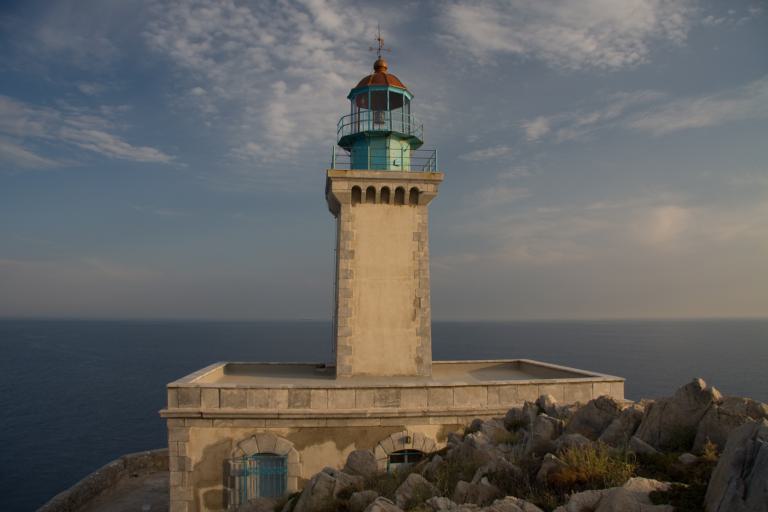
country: GR
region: Peloponnese
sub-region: Nomos Lakonias
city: Gytheio
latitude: 36.3867
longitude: 22.4828
